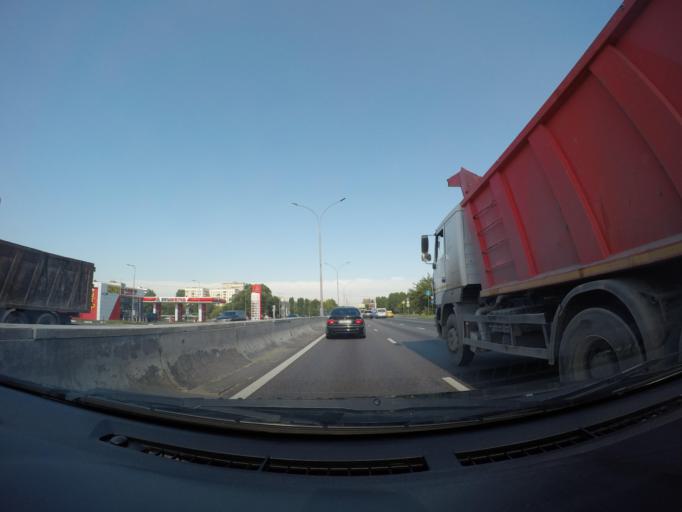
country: RU
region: Moscow
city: Vykhino-Zhulebino
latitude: 55.6943
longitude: 37.8126
